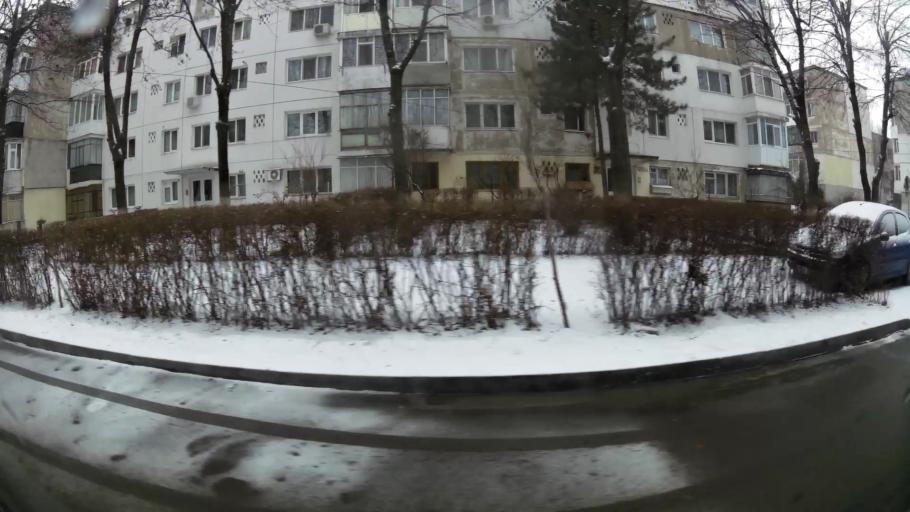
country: RO
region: Prahova
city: Ploiesti
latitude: 44.9322
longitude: 25.9973
